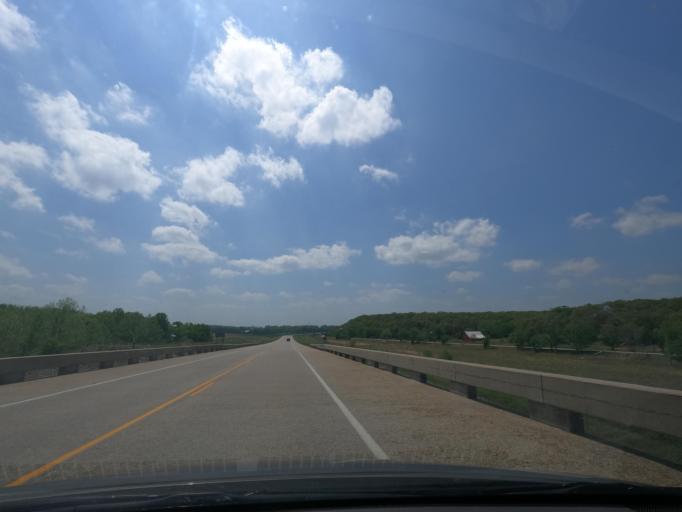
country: US
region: Kansas
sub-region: Wilson County
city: Fredonia
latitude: 37.6198
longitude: -95.9899
